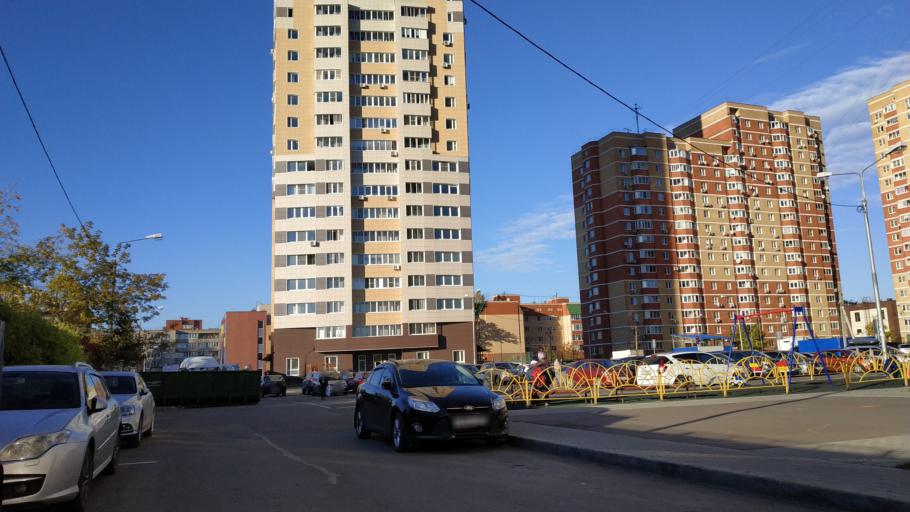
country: RU
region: Moskovskaya
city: Lobnya
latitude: 56.0052
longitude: 37.4644
